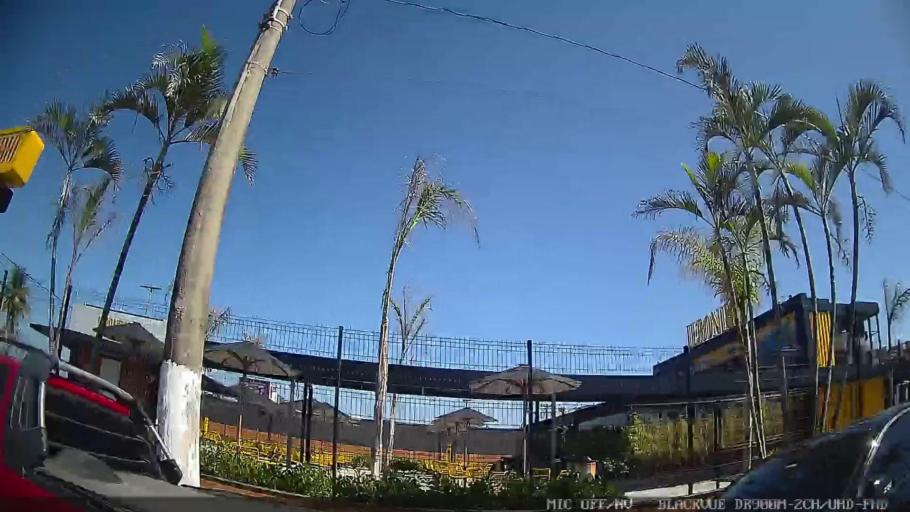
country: BR
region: Sao Paulo
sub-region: Guaruja
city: Guaruja
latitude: -23.9869
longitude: -46.2309
